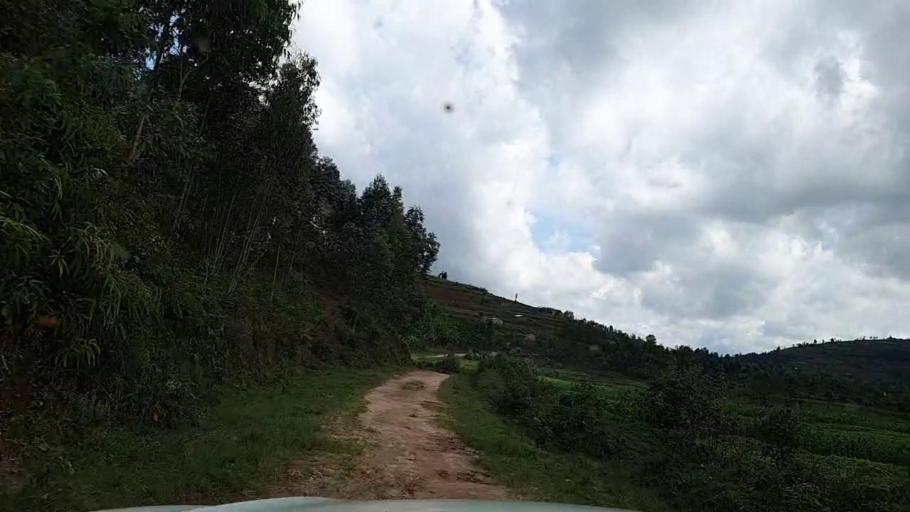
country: RW
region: Southern Province
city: Gikongoro
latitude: -2.3903
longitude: 29.5493
